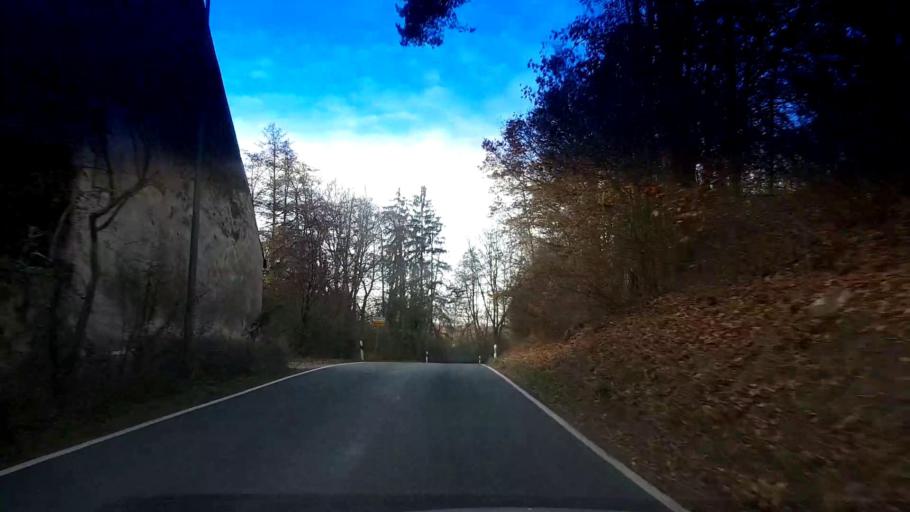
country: DE
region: Bavaria
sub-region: Upper Franconia
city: Walsdorf
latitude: 49.8774
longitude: 10.7642
